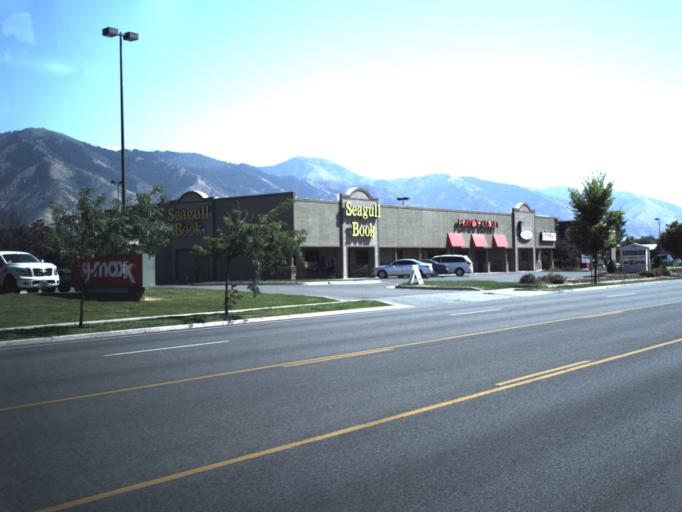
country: US
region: Utah
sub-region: Cache County
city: Logan
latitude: 41.7529
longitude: -111.8346
